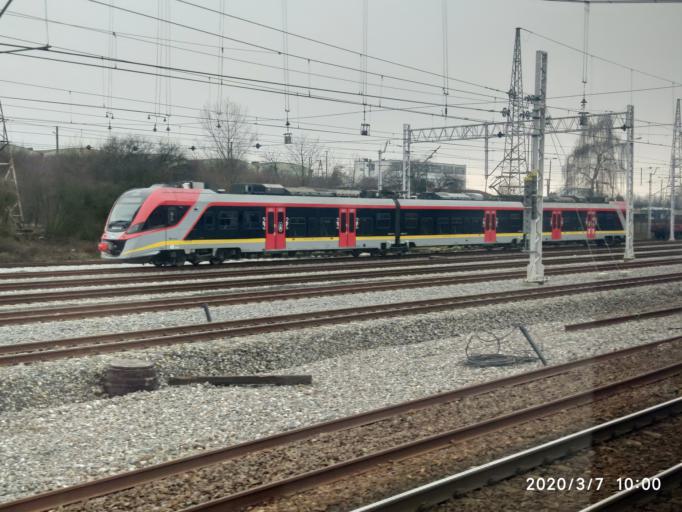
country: PL
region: Lodz Voivodeship
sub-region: Powiat kutnowski
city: Kutno
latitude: 52.2302
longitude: 19.3395
